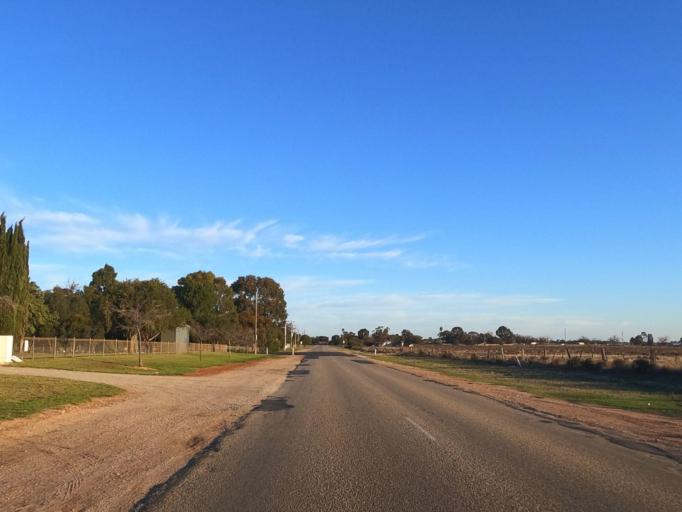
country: AU
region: Victoria
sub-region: Swan Hill
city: Swan Hill
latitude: -35.3549
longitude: 143.5527
